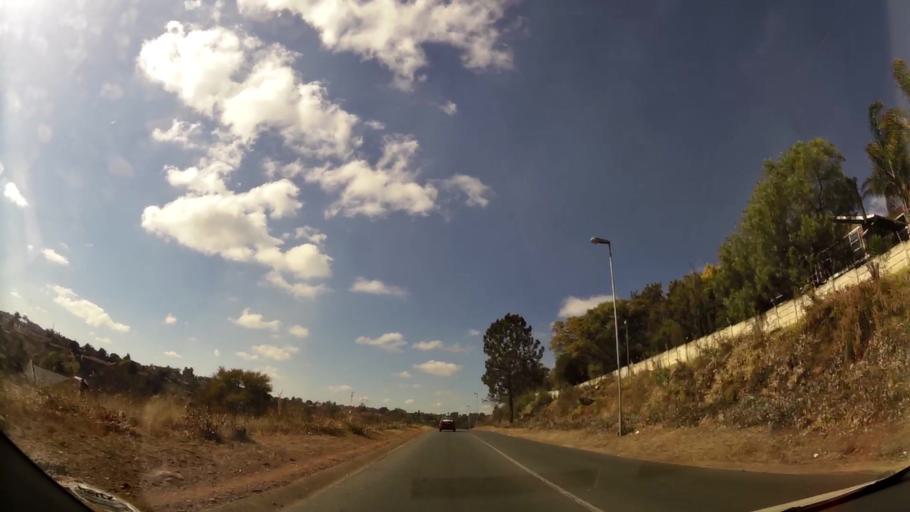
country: ZA
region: Gauteng
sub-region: City of Johannesburg Metropolitan Municipality
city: Roodepoort
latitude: -26.1131
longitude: 27.8425
